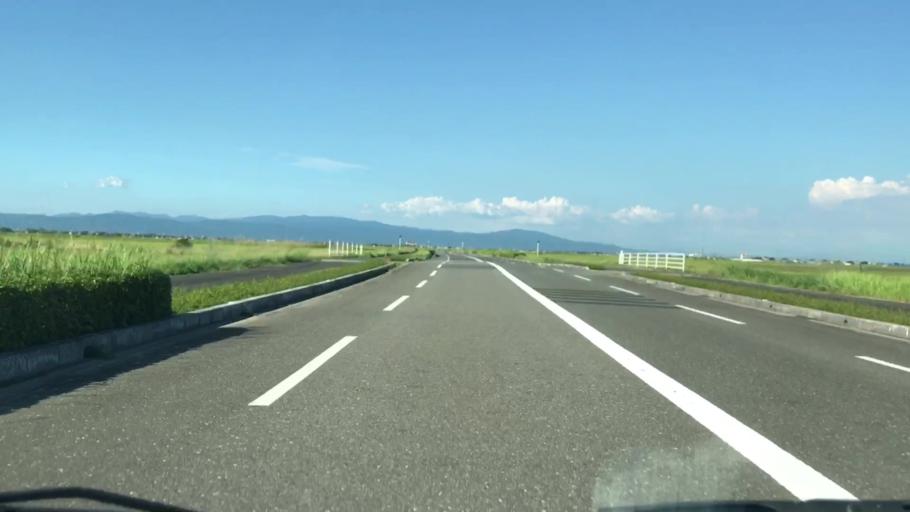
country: JP
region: Saga Prefecture
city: Okawa
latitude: 33.1661
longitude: 130.2925
